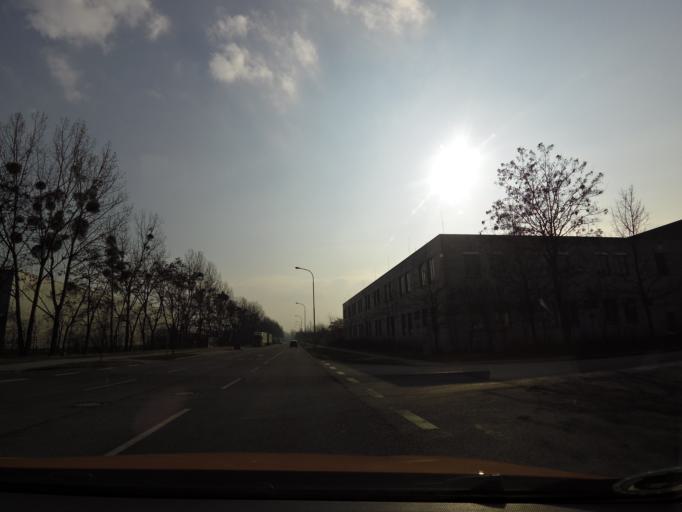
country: DE
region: Brandenburg
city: Grossbeeren
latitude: 52.3767
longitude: 13.3114
